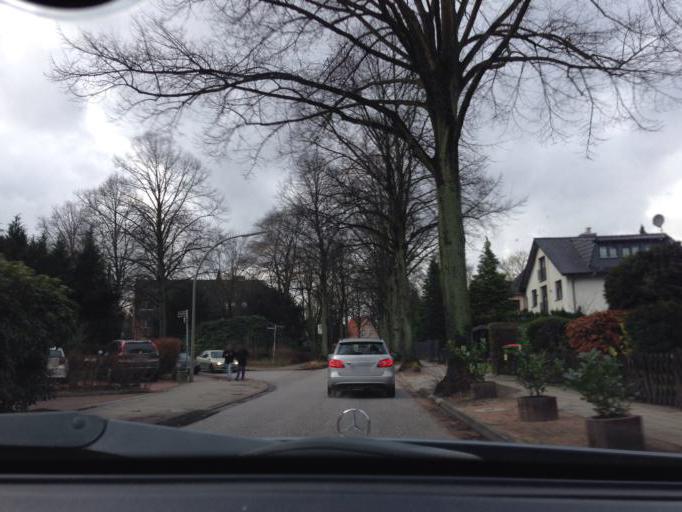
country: DE
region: Hamburg
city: Farmsen-Berne
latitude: 53.6056
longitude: 10.1473
